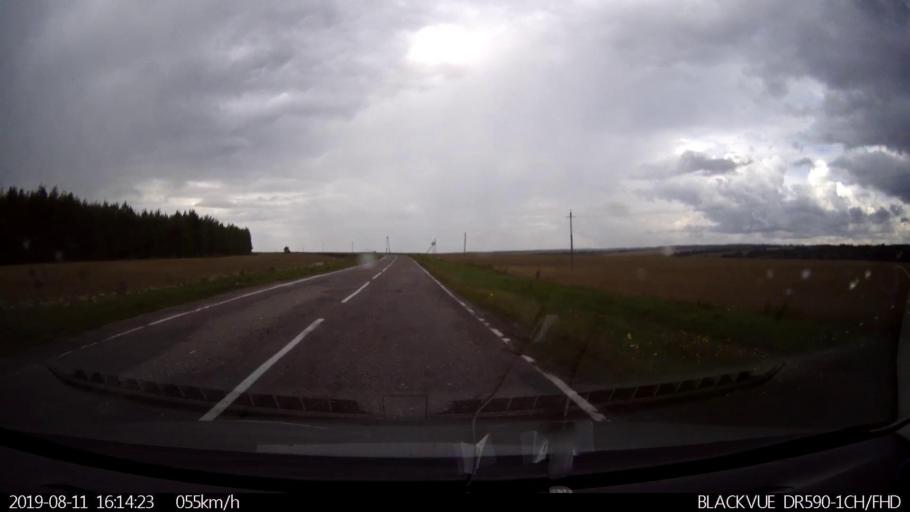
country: RU
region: Ulyanovsk
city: Ignatovka
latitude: 54.0275
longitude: 47.6342
